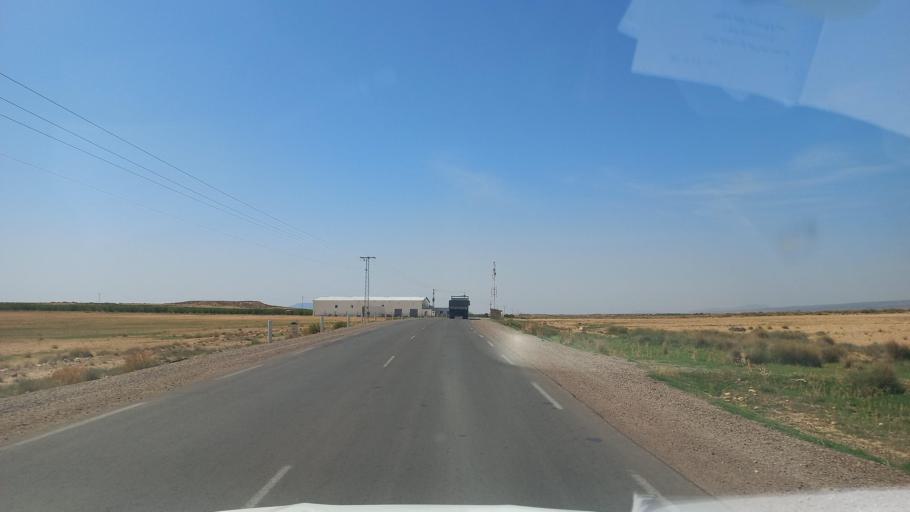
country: TN
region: Al Qasrayn
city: Sbiba
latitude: 35.3785
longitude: 9.1068
